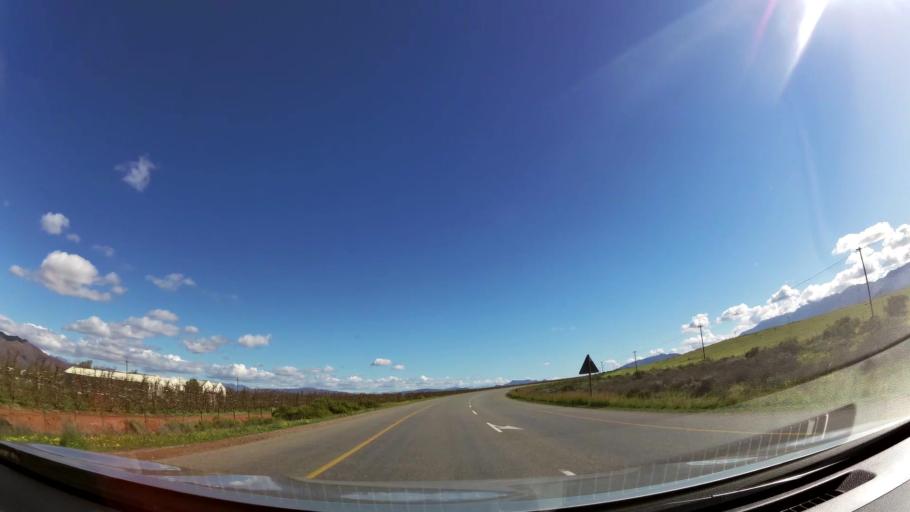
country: ZA
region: Western Cape
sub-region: Cape Winelands District Municipality
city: Ashton
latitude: -33.8394
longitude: 20.0122
